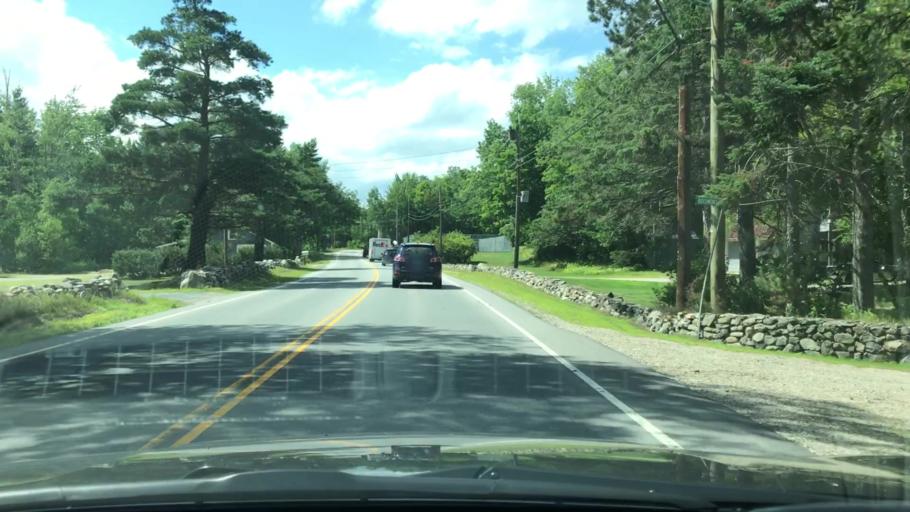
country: US
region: New Hampshire
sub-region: Coos County
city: Jefferson
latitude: 44.3700
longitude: -71.4042
